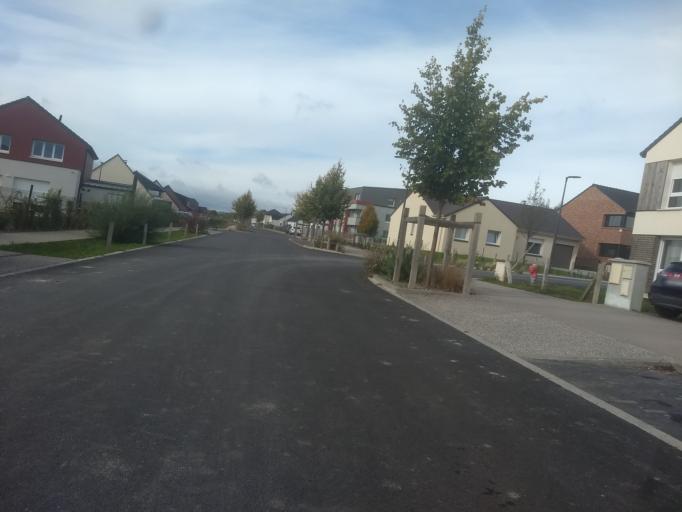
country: FR
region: Nord-Pas-de-Calais
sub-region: Departement du Pas-de-Calais
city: Dainville
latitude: 50.2893
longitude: 2.7343
